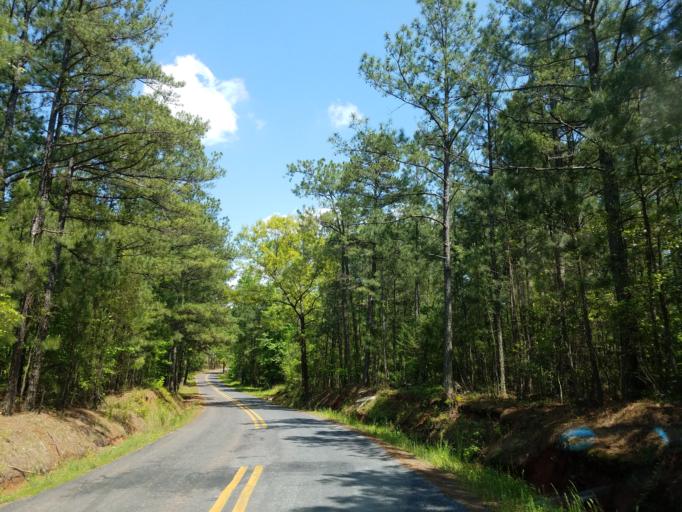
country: US
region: Georgia
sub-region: Monroe County
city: Forsyth
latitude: 33.1415
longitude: -84.0001
